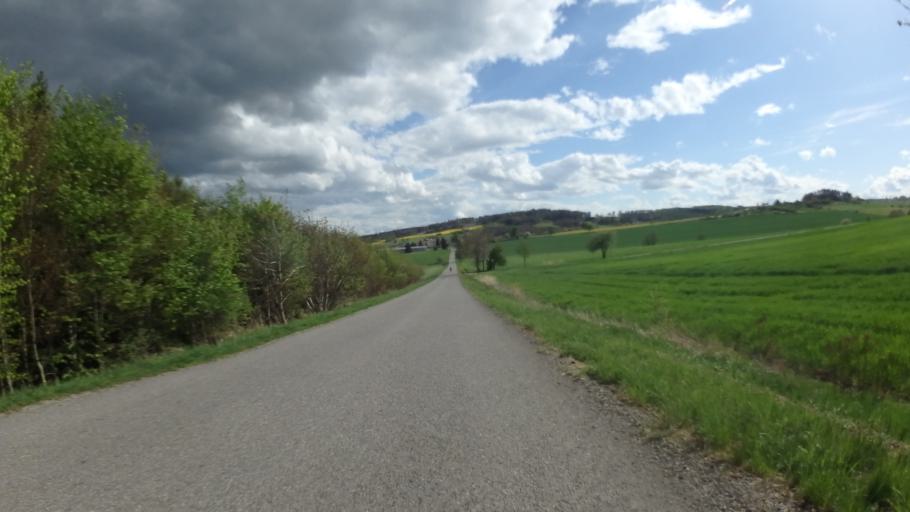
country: CZ
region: Vysocina
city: Merin
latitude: 49.3563
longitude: 15.8781
